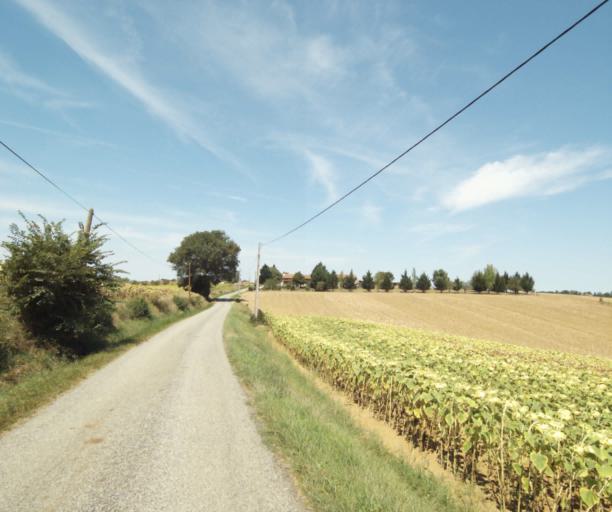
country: FR
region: Midi-Pyrenees
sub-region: Departement de l'Ariege
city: Lezat-sur-Leze
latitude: 43.2840
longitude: 1.3033
